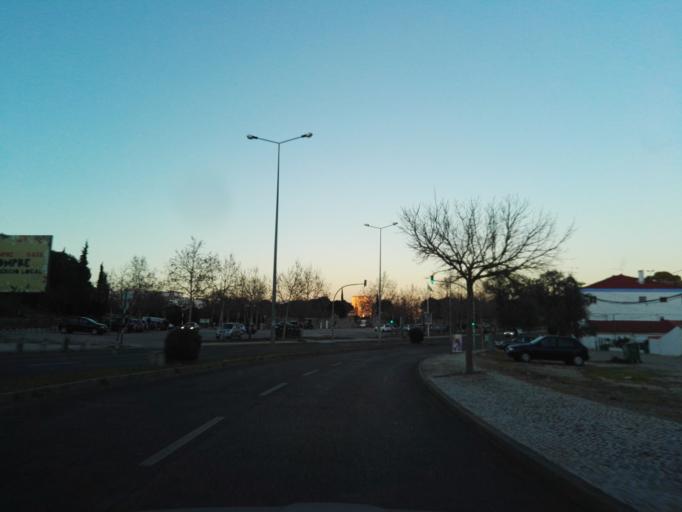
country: PT
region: Setubal
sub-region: Almada
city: Pragal
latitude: 38.6620
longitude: -9.1659
